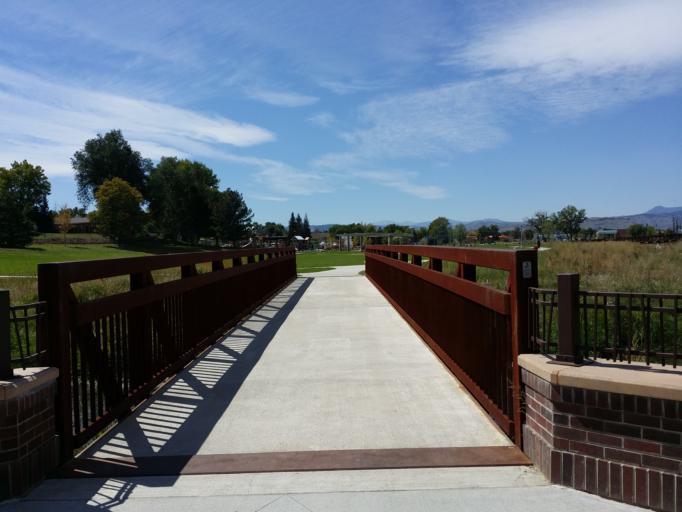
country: US
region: Colorado
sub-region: Jefferson County
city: Arvada
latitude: 39.8037
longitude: -105.0953
